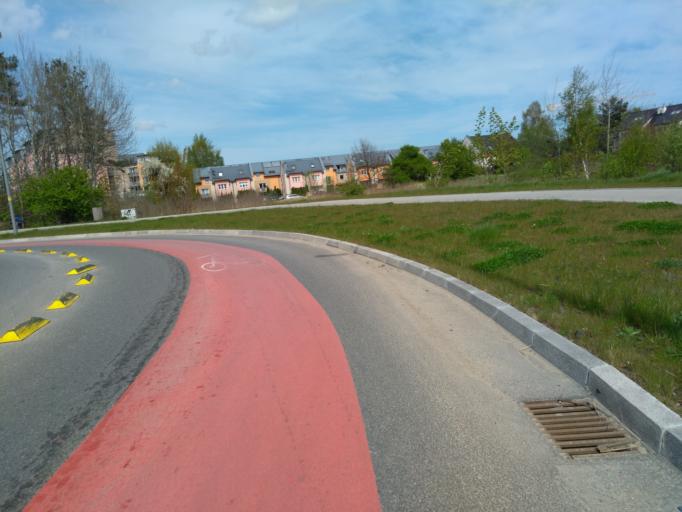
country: PL
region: Pomeranian Voivodeship
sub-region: Gdynia
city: Wielki Kack
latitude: 54.4161
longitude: 18.4799
